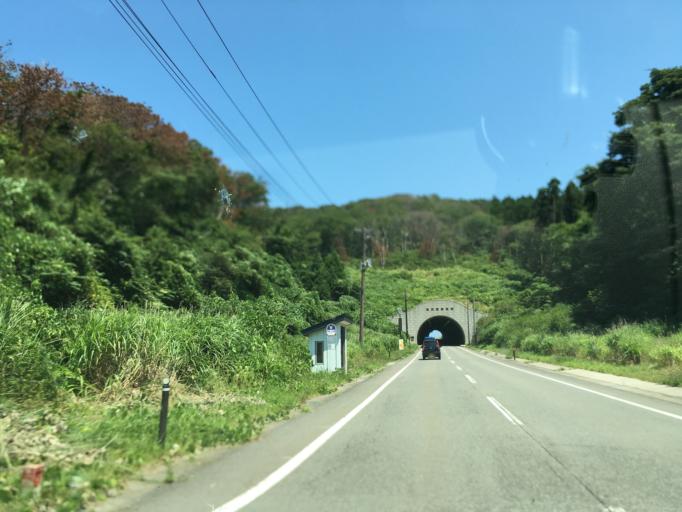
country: JP
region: Akita
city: Tenno
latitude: 39.9615
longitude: 139.7235
